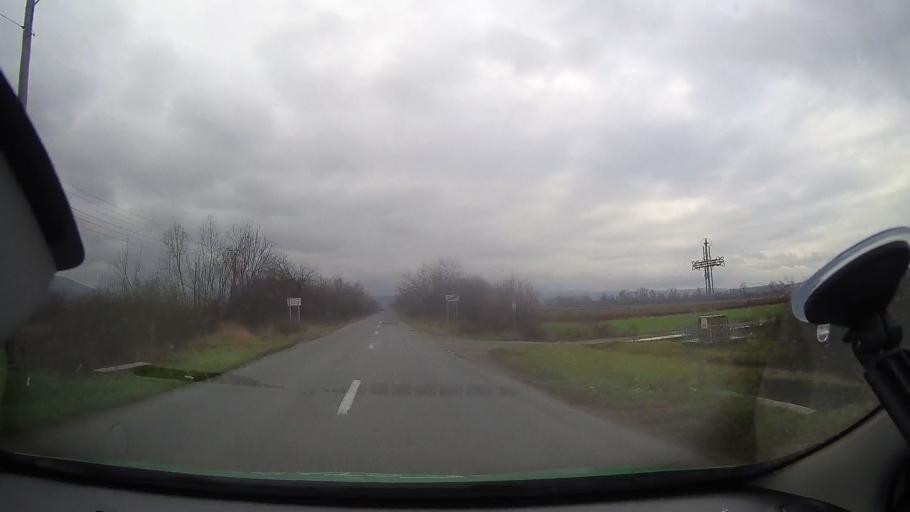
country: RO
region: Arad
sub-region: Comuna Sebis
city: Sebis
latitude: 46.3593
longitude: 22.1306
